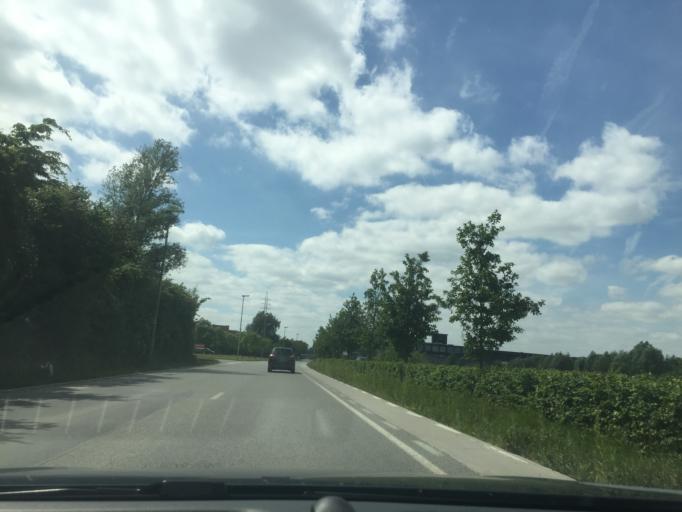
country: BE
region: Flanders
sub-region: Provincie West-Vlaanderen
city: Harelbeke
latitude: 50.8277
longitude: 3.3078
